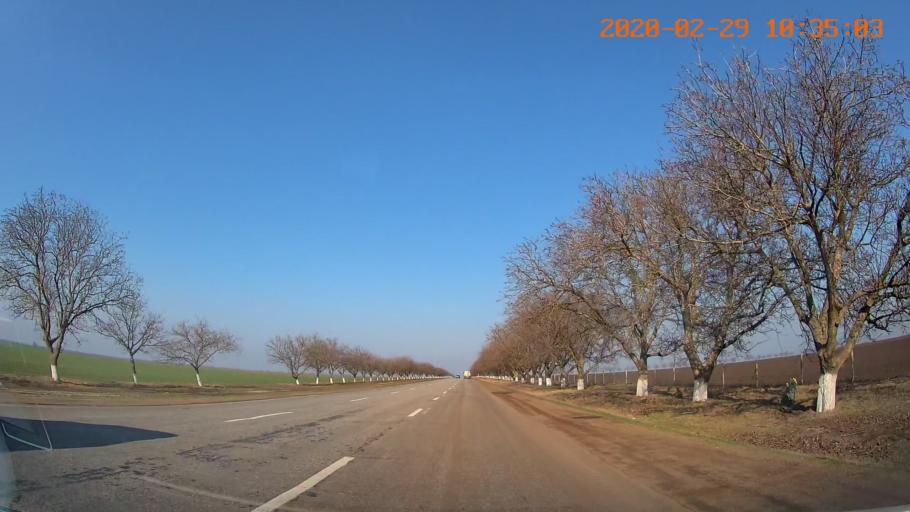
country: MD
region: Anenii Noi
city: Varnita
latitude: 46.9820
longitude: 29.5262
